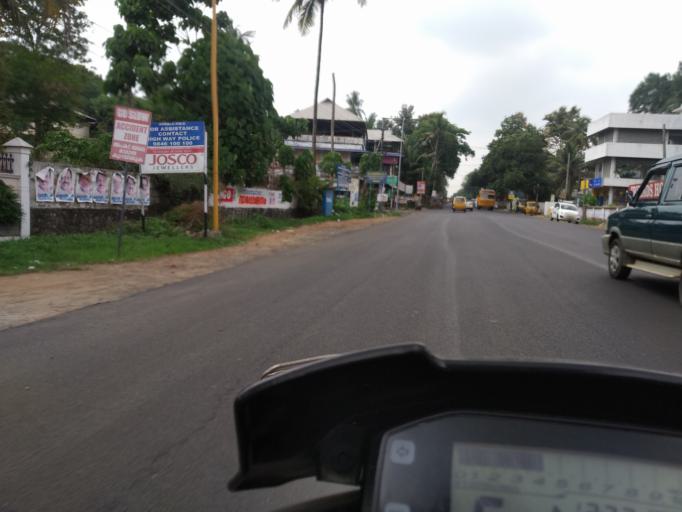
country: IN
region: Kerala
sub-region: Ernakulam
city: Angamali
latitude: 10.1844
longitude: 76.4037
